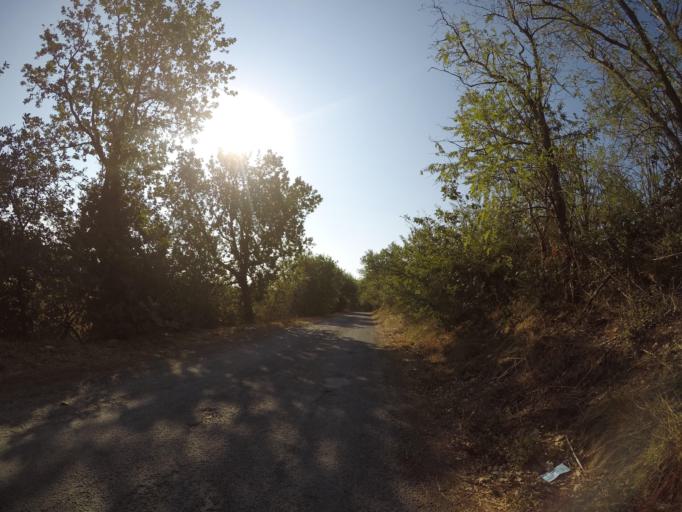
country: FR
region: Languedoc-Roussillon
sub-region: Departement des Pyrenees-Orientales
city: Pollestres
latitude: 42.6678
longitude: 2.8692
